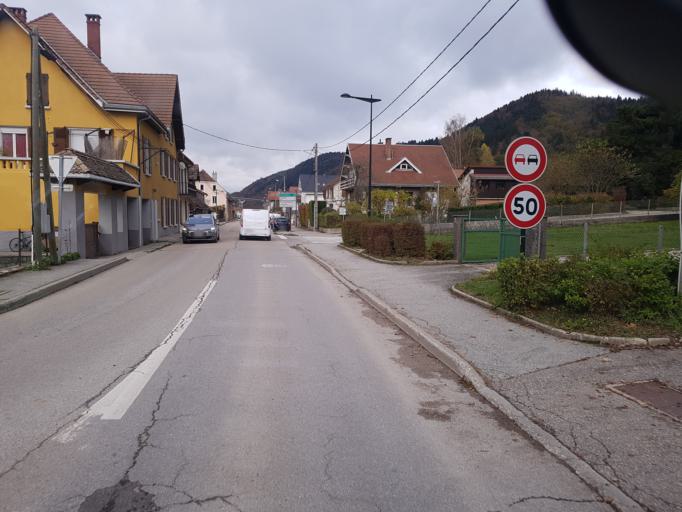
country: FR
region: Rhone-Alpes
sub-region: Departement de l'Isere
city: La Motte-Saint-Martin
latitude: 44.9214
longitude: 5.6366
